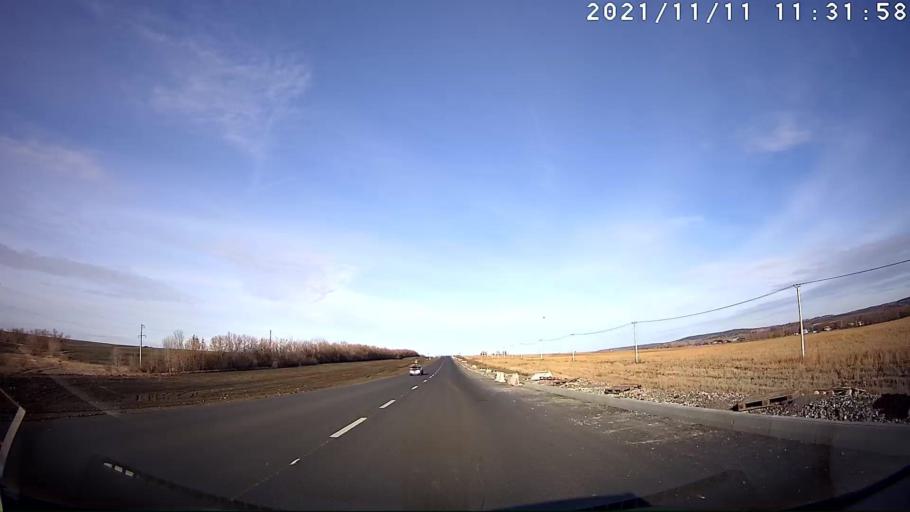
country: RU
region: Samara
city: Varlamovo
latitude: 53.3075
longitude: 48.4489
